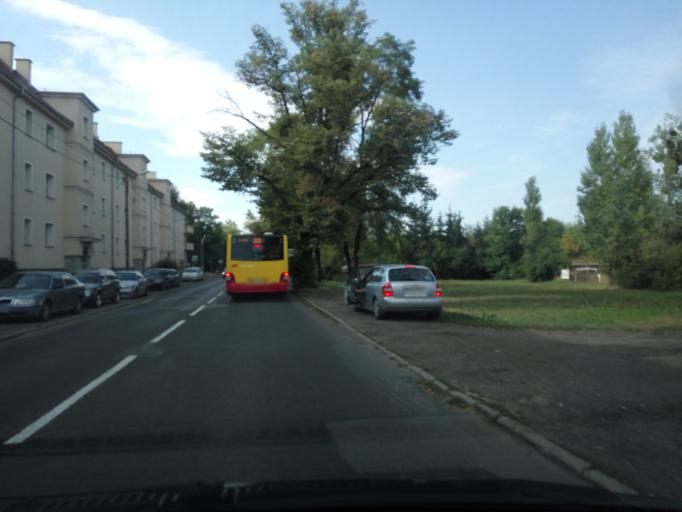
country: PL
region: Lower Silesian Voivodeship
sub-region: Powiat wroclawski
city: Radwanice
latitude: 51.0692
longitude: 17.0806
